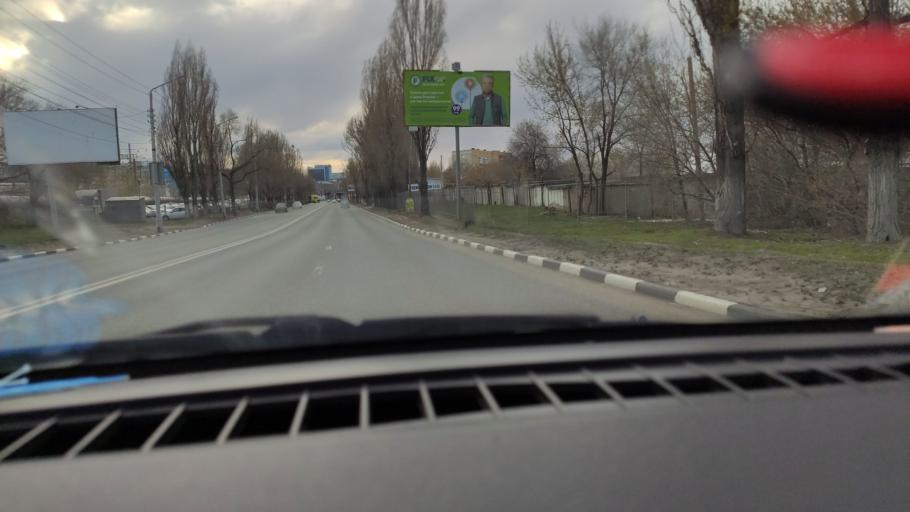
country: RU
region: Saratov
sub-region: Saratovskiy Rayon
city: Saratov
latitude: 51.5810
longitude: 45.9769
